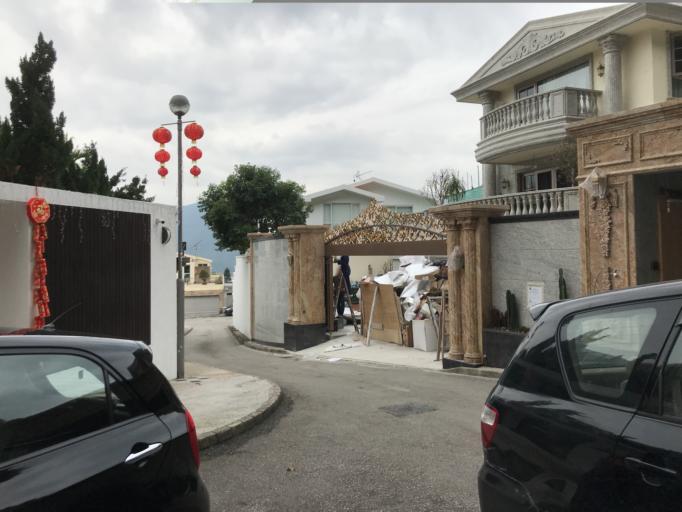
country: HK
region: Tai Po
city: Tai Po
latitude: 22.4640
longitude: 114.1616
